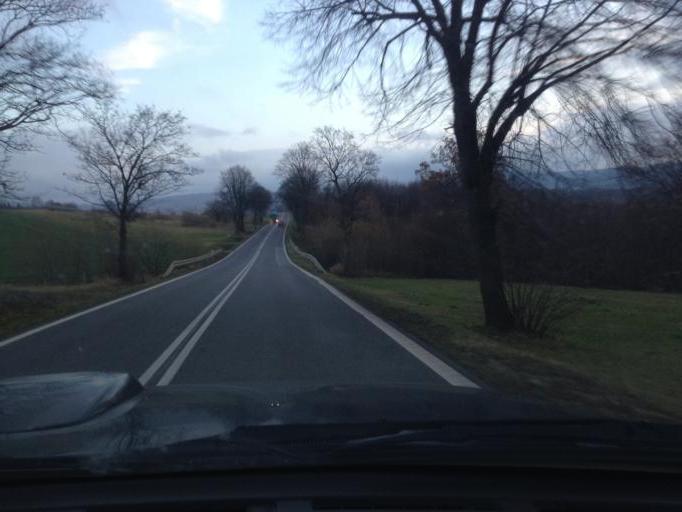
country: PL
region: Subcarpathian Voivodeship
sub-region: Powiat jasielski
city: Nowy Zmigrod
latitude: 49.6294
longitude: 21.5312
